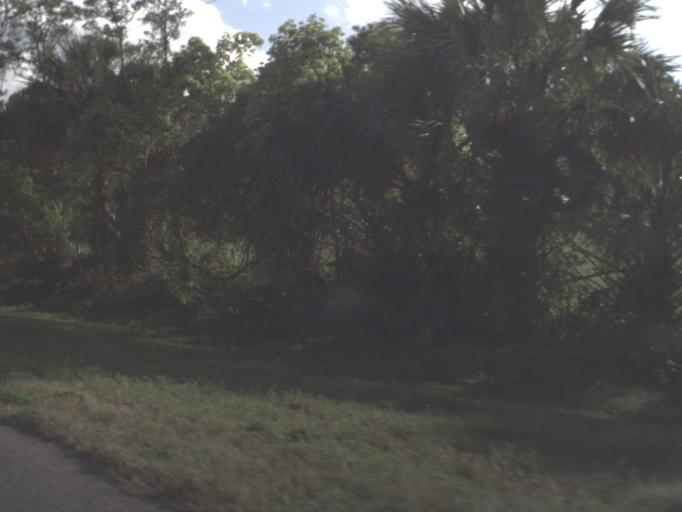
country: US
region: Florida
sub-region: Flagler County
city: Bunnell
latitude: 29.3370
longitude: -81.3108
